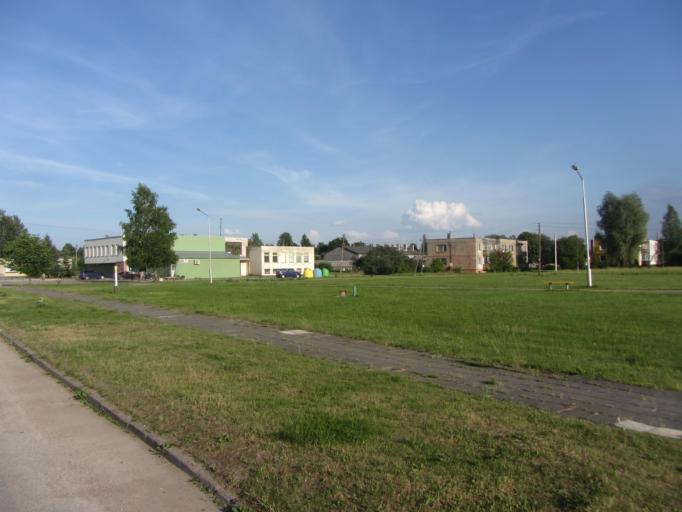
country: LT
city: Kaisiadorys
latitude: 55.0835
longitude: 24.5344
